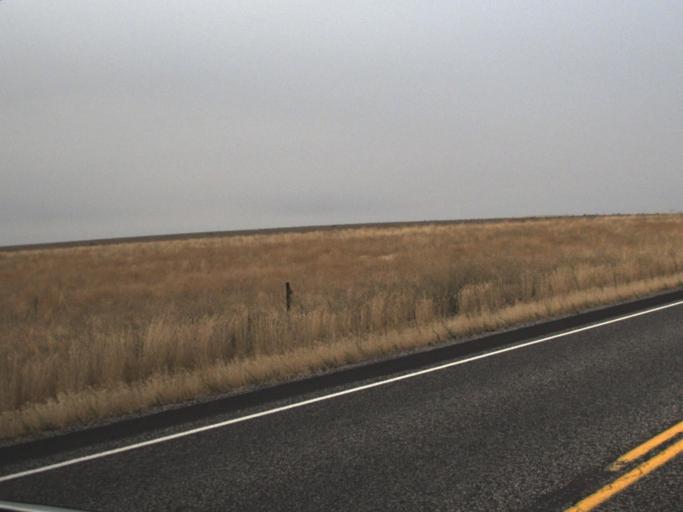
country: US
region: Washington
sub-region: Benton County
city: Benton City
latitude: 46.1787
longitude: -119.6009
